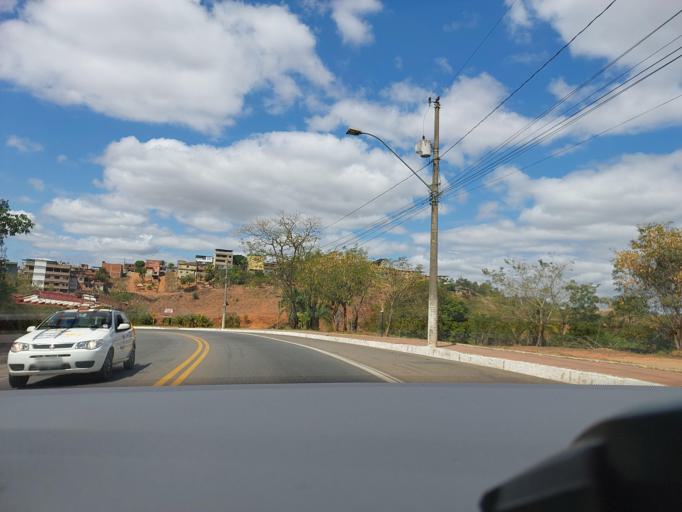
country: BR
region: Minas Gerais
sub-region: Muriae
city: Muriae
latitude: -21.1287
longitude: -42.3495
